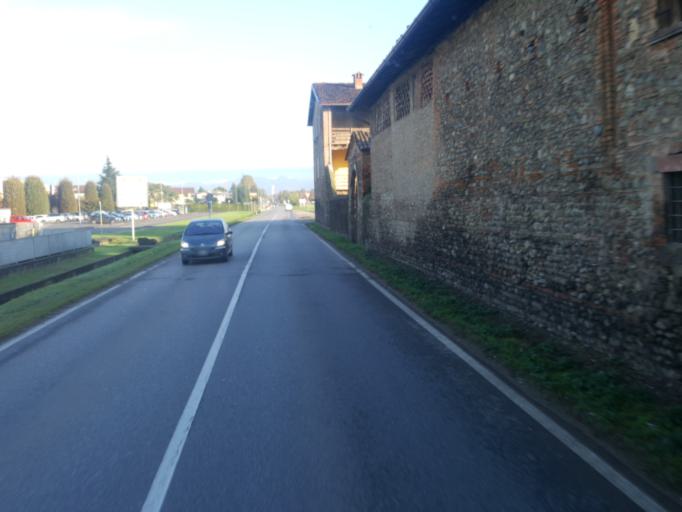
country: IT
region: Lombardy
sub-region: Provincia di Bergamo
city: Cologno al Serio
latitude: 45.5665
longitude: 9.7082
